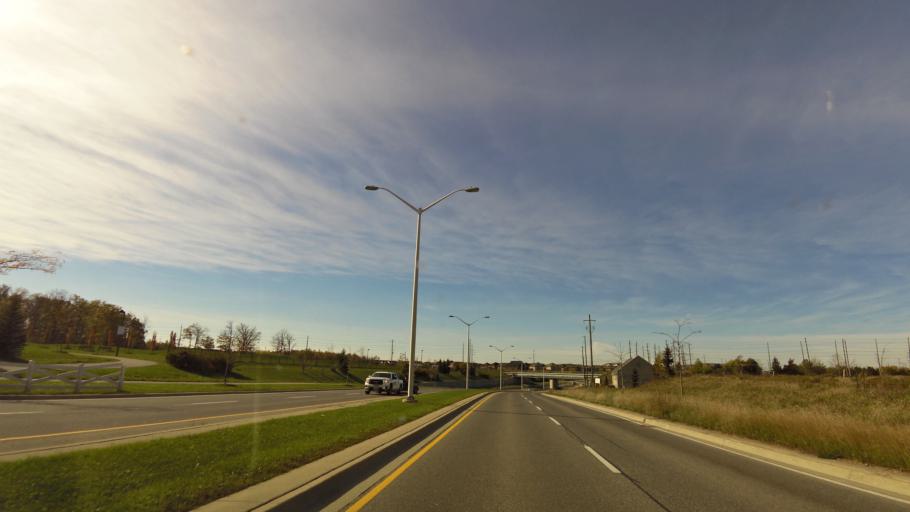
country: CA
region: Ontario
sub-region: Halton
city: Milton
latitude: 43.5343
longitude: -79.8474
